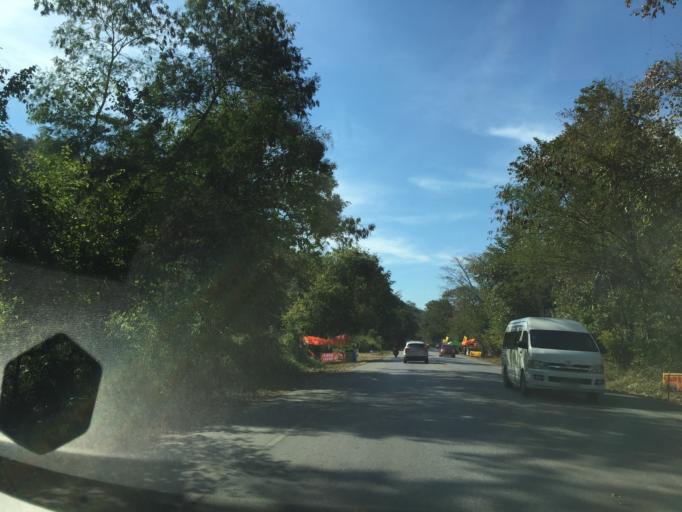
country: TH
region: Loei
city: Wang Saphung
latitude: 17.2884
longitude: 101.8315
